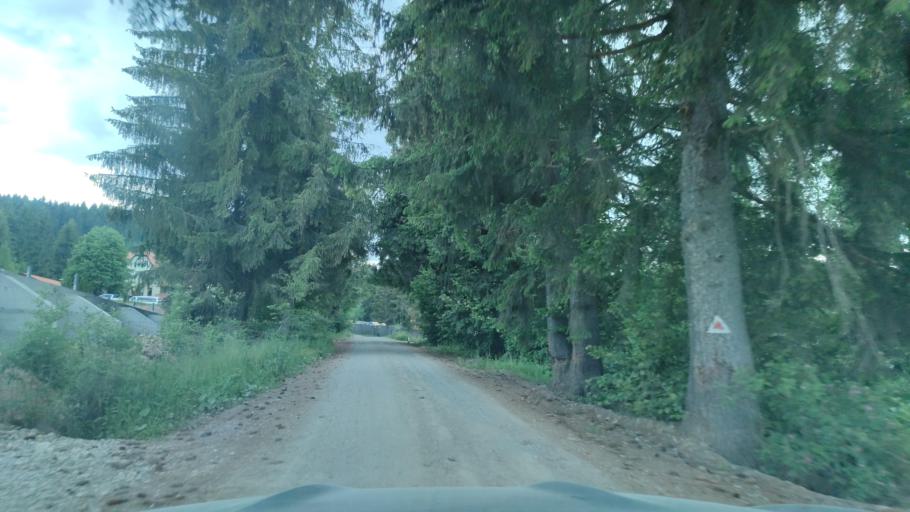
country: RO
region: Harghita
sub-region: Comuna Joseni
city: Joseni
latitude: 46.6683
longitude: 25.3776
